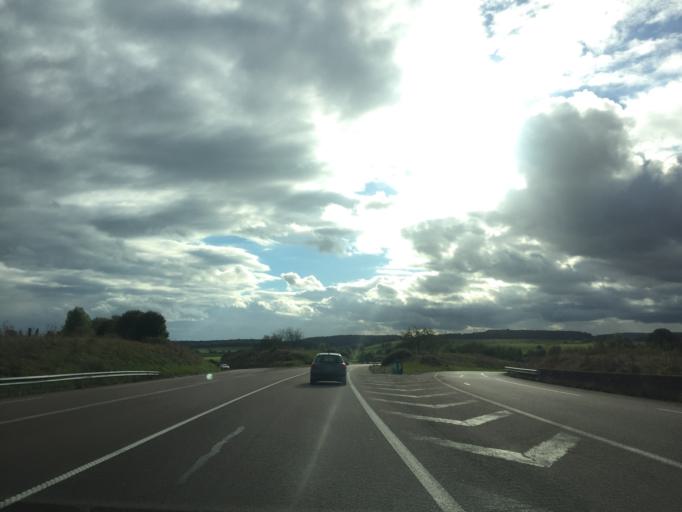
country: FR
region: Lorraine
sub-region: Departement des Vosges
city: Chatenois
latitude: 48.2942
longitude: 5.9035
